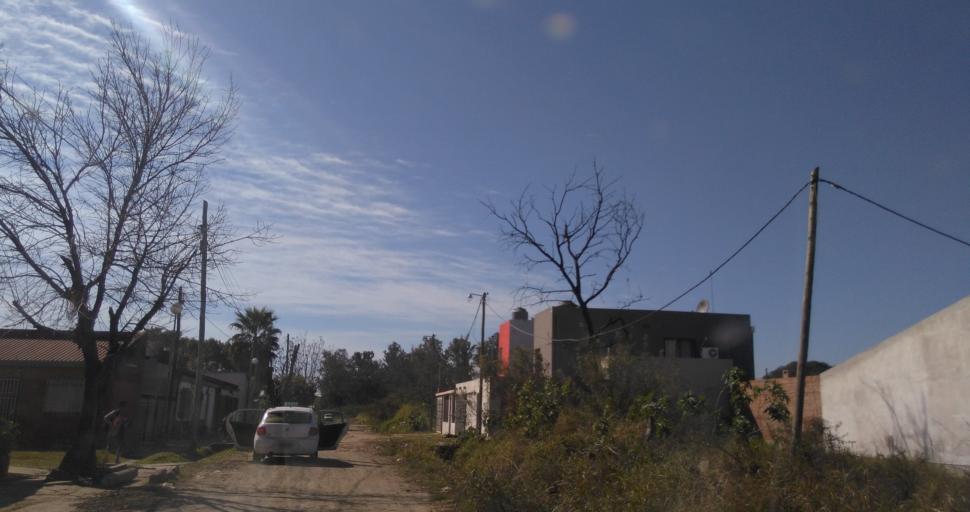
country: AR
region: Chaco
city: Fontana
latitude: -27.4484
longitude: -59.0312
